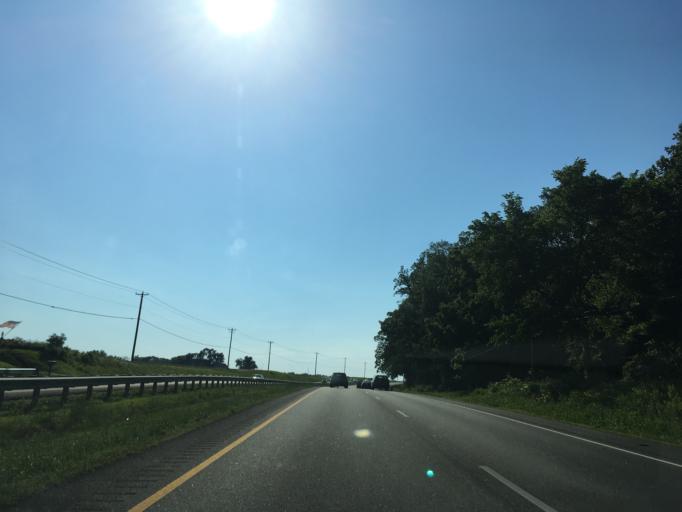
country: US
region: Maryland
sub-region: Queen Anne's County
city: Centreville
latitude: 38.9655
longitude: -76.1105
